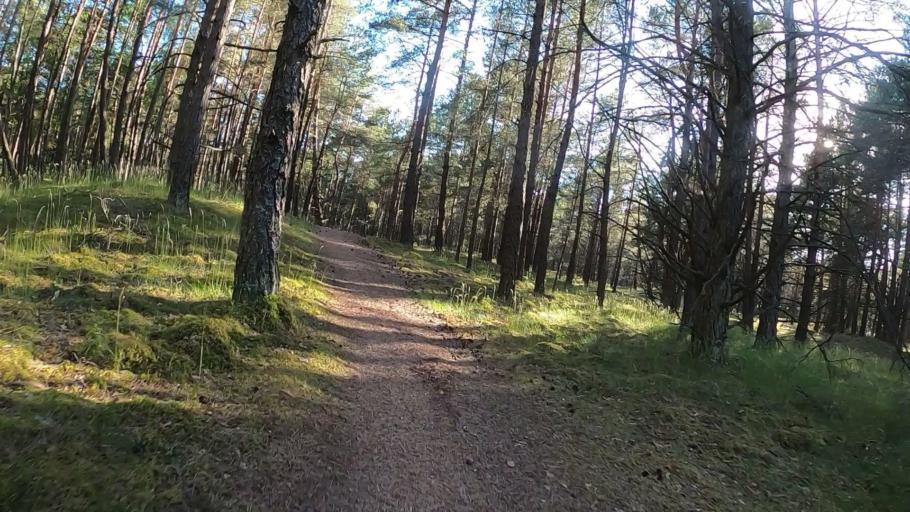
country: LV
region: Carnikava
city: Carnikava
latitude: 57.1343
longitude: 24.2327
